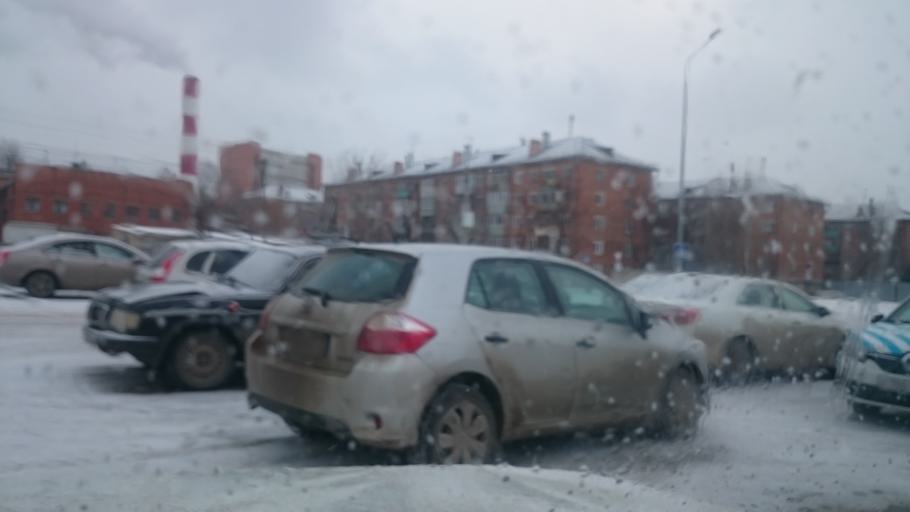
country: RU
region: Tula
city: Tula
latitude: 54.1994
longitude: 37.5990
